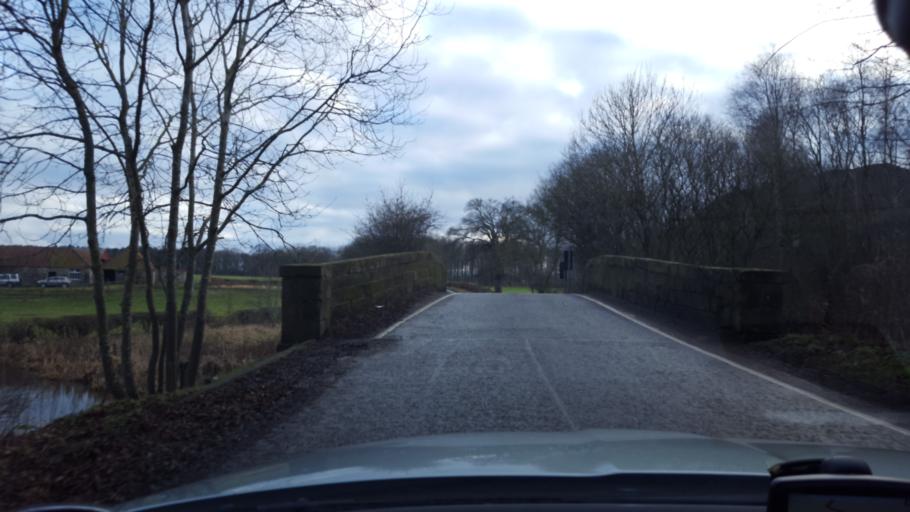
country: GB
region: Scotland
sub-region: West Lothian
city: Broxburn
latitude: 55.9745
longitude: -3.5085
